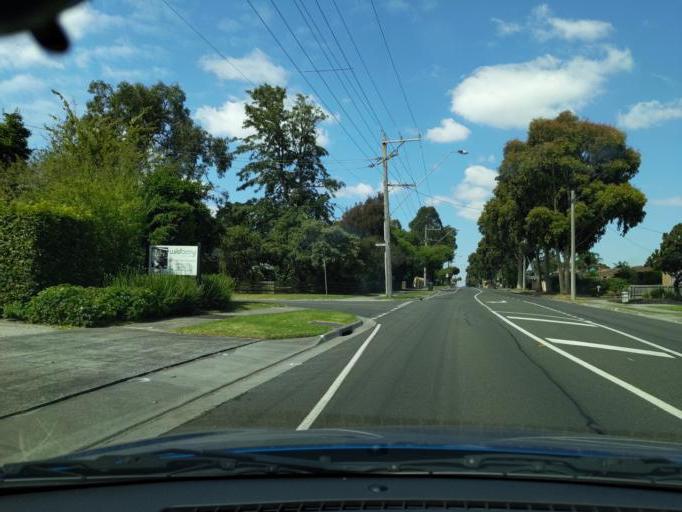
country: AU
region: Victoria
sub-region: Knox
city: Rowville
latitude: -37.9215
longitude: 145.2452
